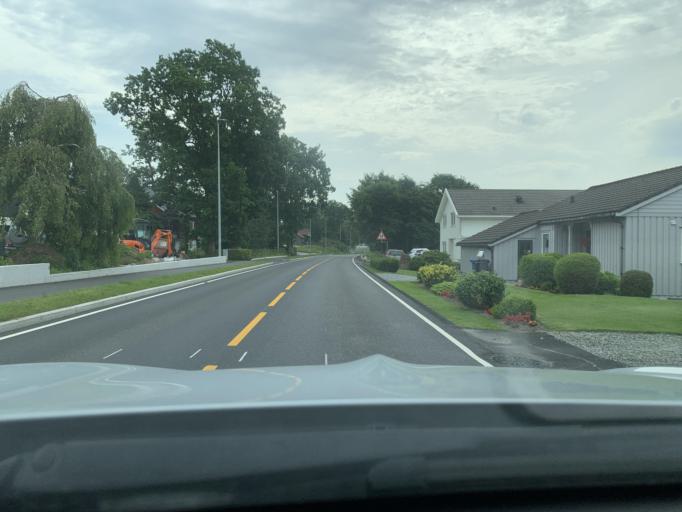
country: NO
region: Rogaland
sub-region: Sandnes
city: Sandnes
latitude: 58.7756
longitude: 5.7225
